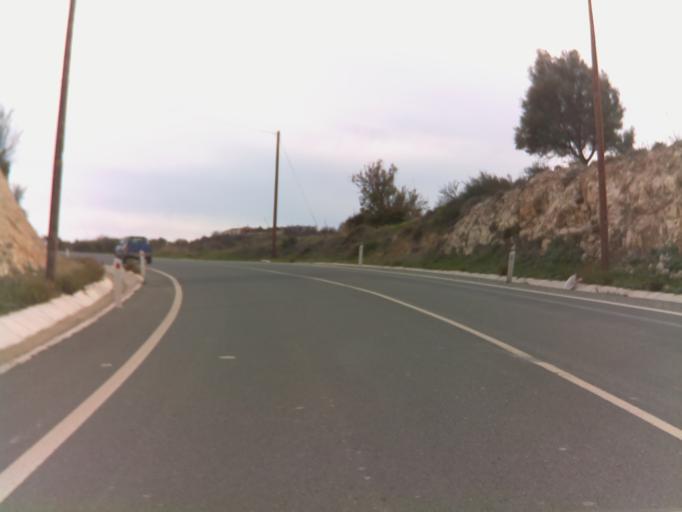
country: CY
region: Pafos
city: Polis
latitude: 34.9935
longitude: 32.4046
